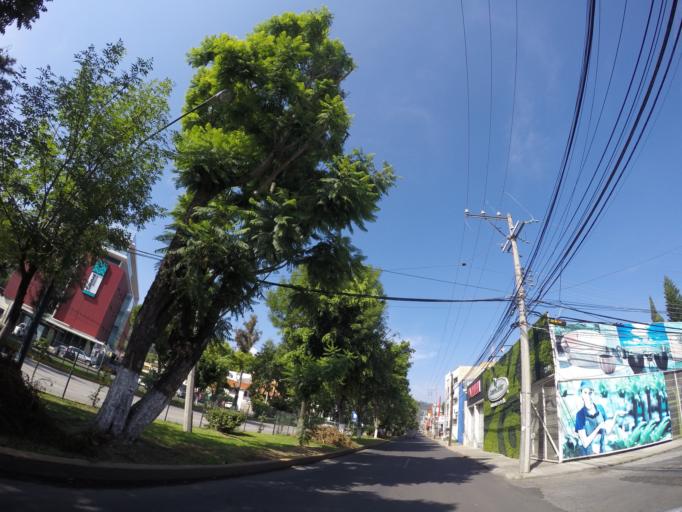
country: MX
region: Michoacan
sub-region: Morelia
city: Montana Monarca (Punta Altozano)
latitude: 19.6860
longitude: -101.1636
